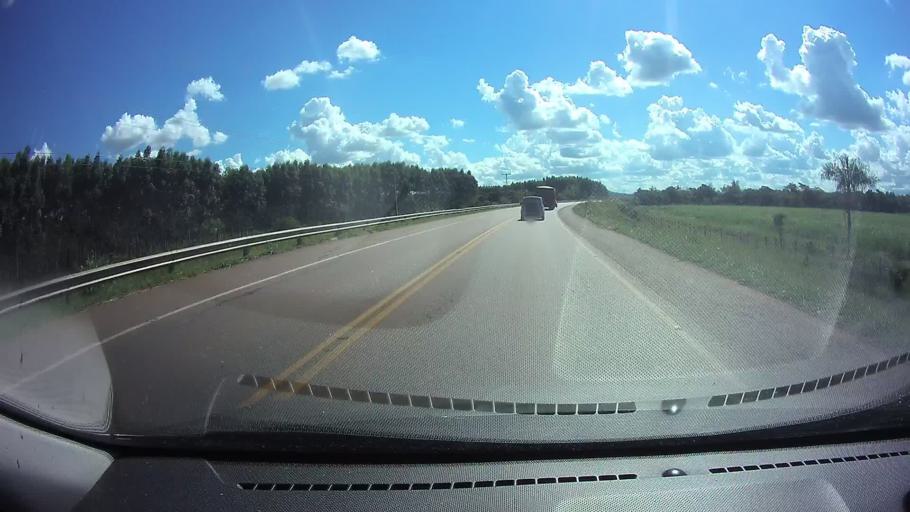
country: PY
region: Guaira
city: Coronel Martinez
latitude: -25.7641
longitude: -56.7261
